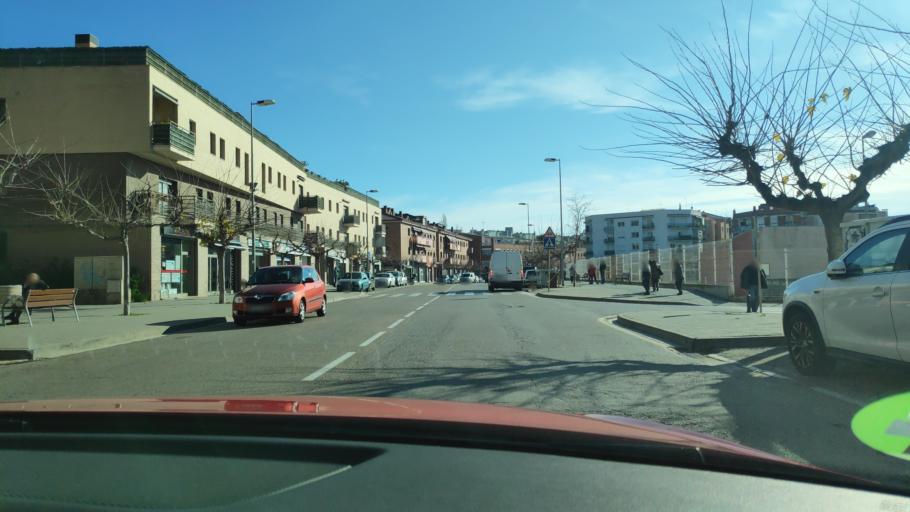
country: ES
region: Catalonia
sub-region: Provincia de Girona
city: Lloret de Mar
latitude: 41.7097
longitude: 2.8396
